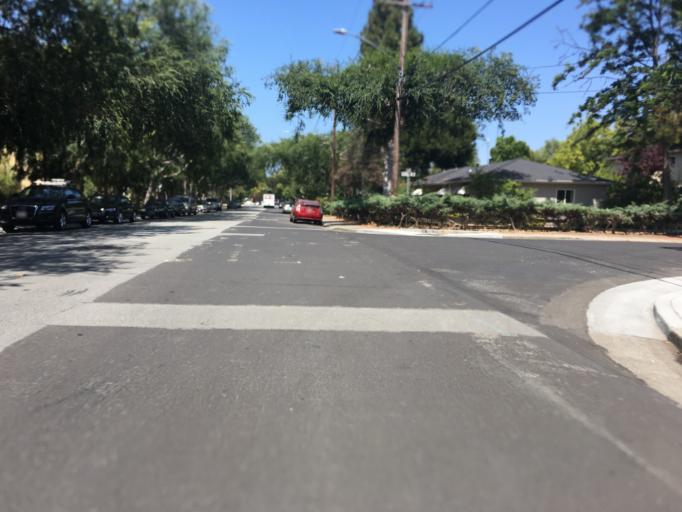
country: US
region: California
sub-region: Santa Clara County
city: Los Altos
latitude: 37.4113
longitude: -122.1200
